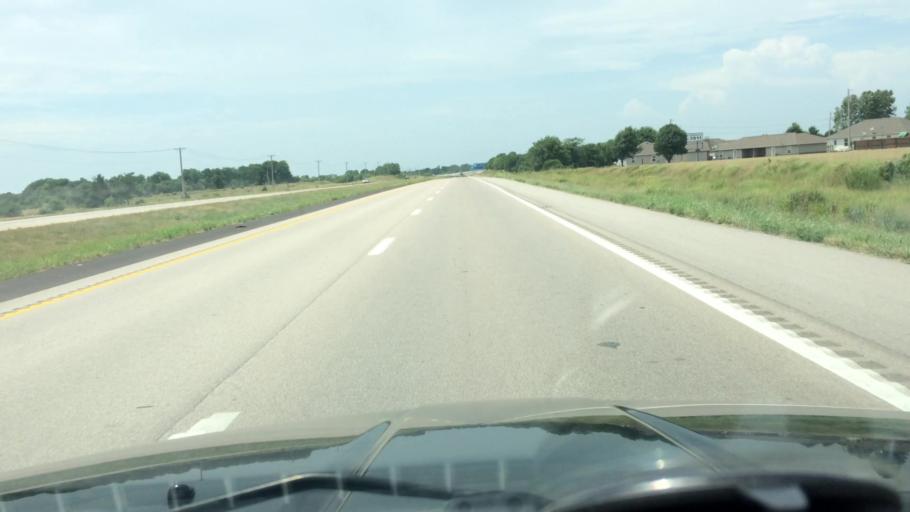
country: US
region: Missouri
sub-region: Polk County
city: Bolivar
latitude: 37.5865
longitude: -93.4199
